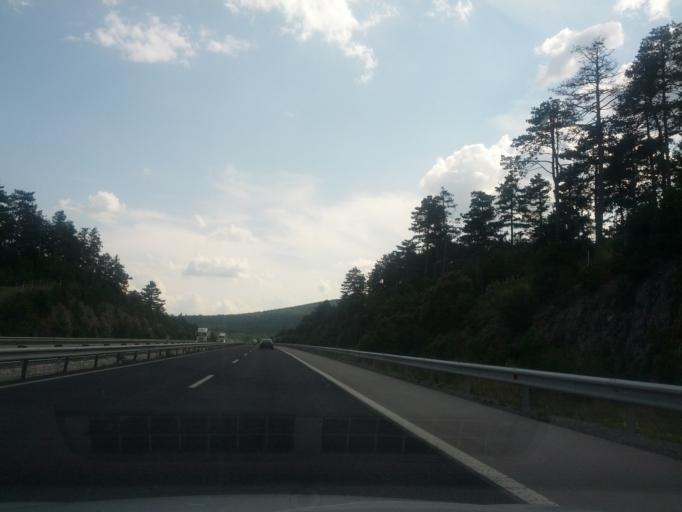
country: SI
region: Divaca
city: Divaca
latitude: 45.6594
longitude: 13.9637
